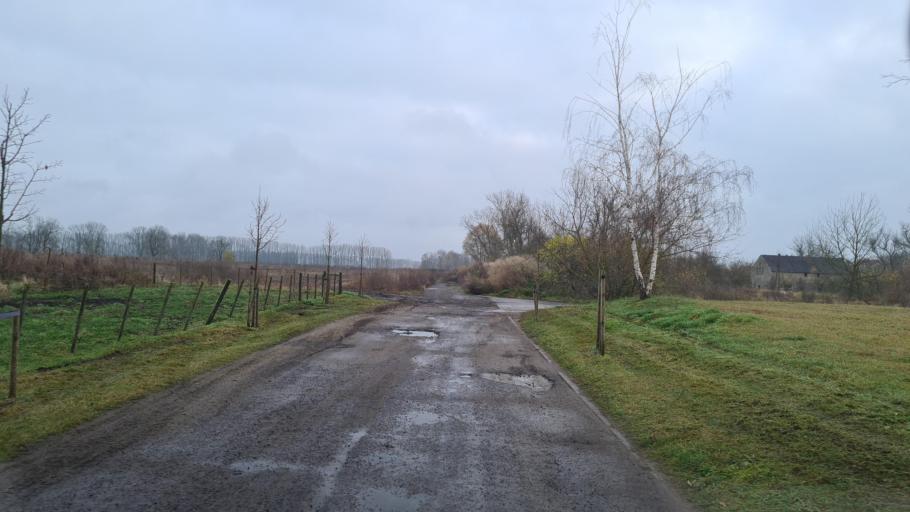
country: DE
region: Brandenburg
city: Nauen
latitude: 52.6640
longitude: 12.8205
